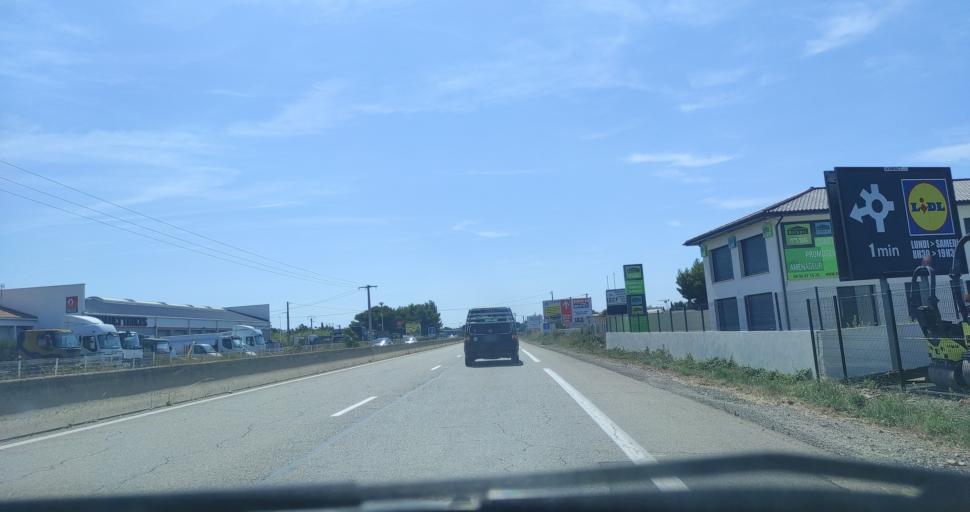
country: FR
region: Provence-Alpes-Cote d'Azur
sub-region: Departement des Bouches-du-Rhone
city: Fos-sur-Mer
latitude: 43.4538
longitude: 4.9291
